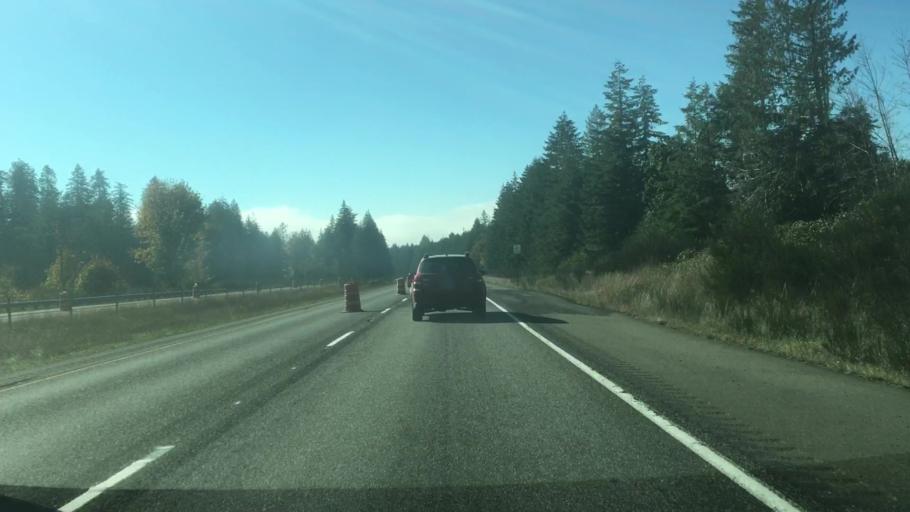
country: US
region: Washington
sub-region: Grays Harbor County
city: McCleary
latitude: 47.0502
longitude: -123.3020
